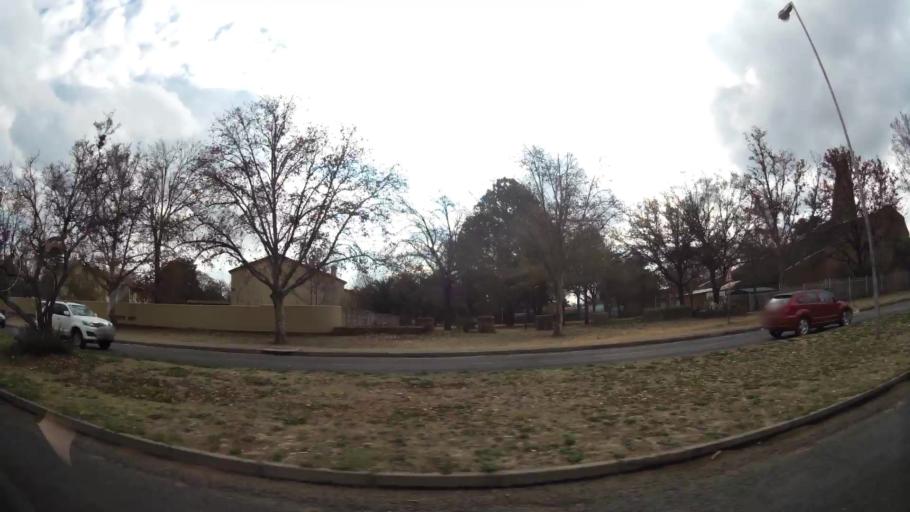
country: ZA
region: Orange Free State
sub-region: Fezile Dabi District Municipality
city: Sasolburg
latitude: -26.8078
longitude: 27.8288
